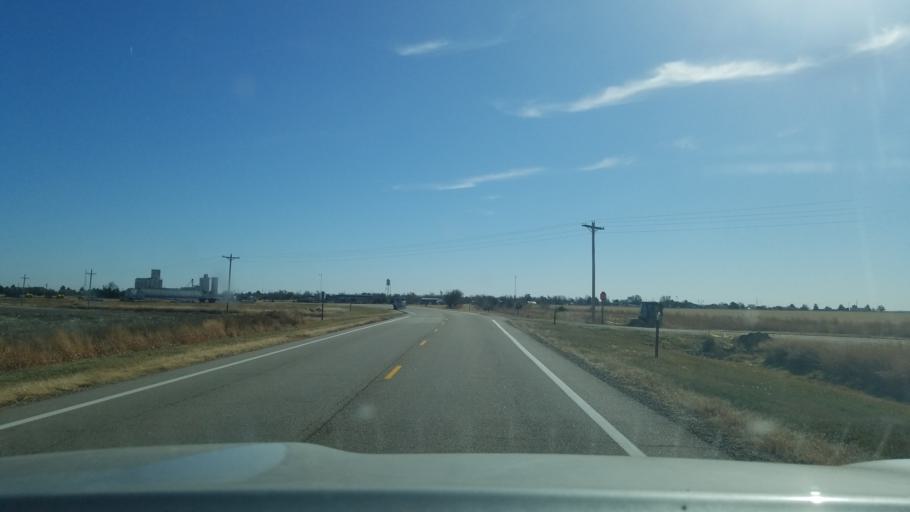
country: US
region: Kansas
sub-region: Kiowa County
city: Greensburg
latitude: 37.5571
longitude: -99.6462
